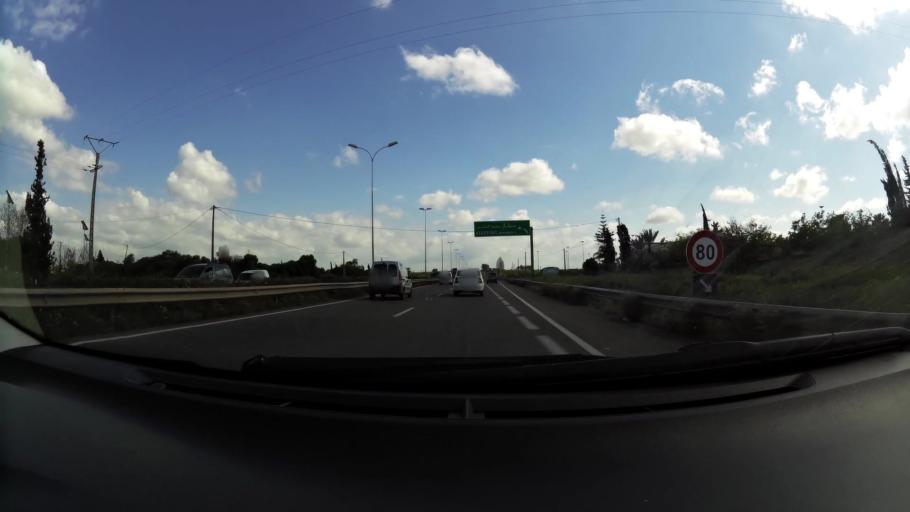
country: MA
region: Chaouia-Ouardigha
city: Nouaseur
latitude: 33.3954
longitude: -7.6205
